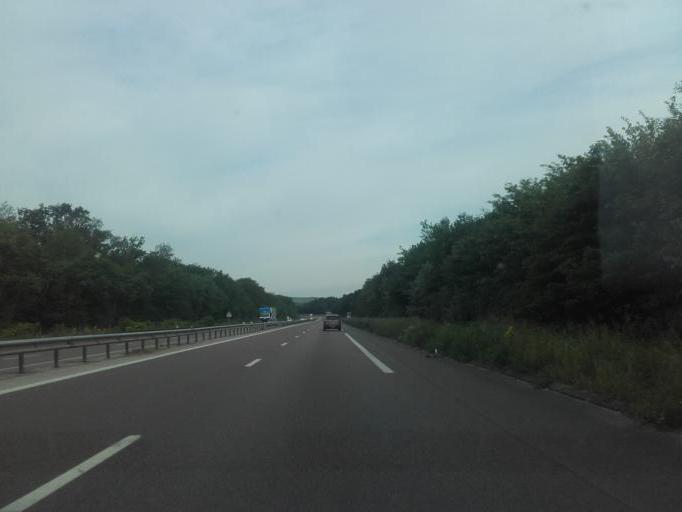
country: FR
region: Bourgogne
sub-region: Departement de Saone-et-Loire
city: Givry
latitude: 46.7595
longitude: 4.7569
